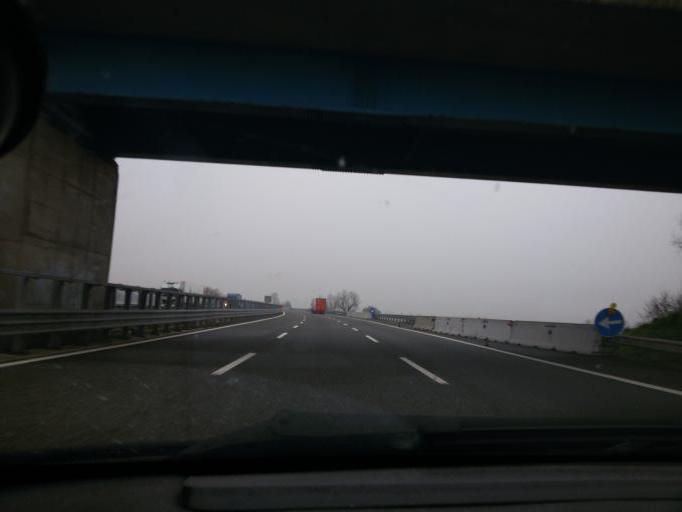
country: IT
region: Piedmont
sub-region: Provincia di Alessandria
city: Villanova Monferrato
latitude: 45.1848
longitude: 8.4972
